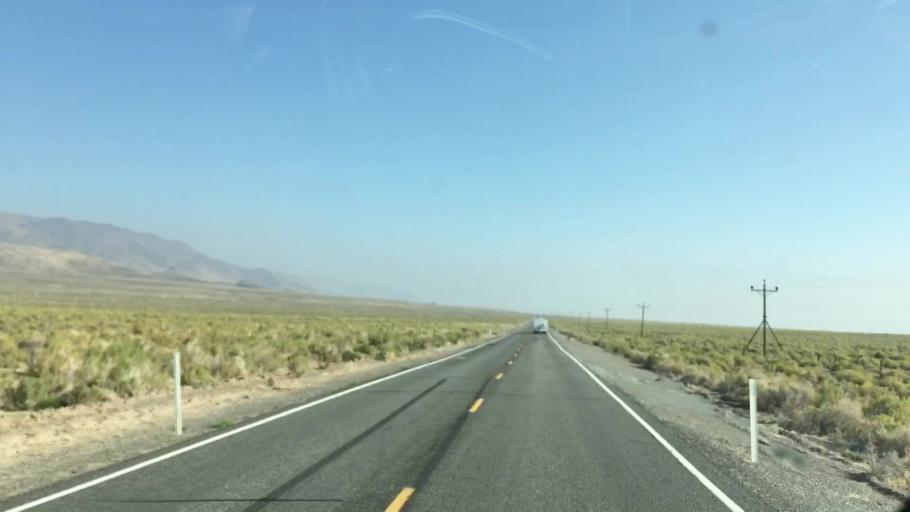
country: US
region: Nevada
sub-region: Lyon County
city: Fernley
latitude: 40.1310
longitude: -119.3686
